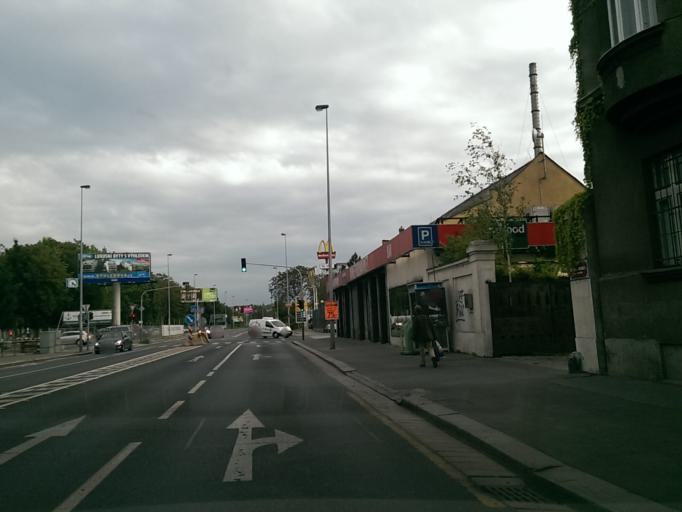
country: CZ
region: Praha
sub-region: Praha 2
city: Vysehrad
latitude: 50.0636
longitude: 14.4105
